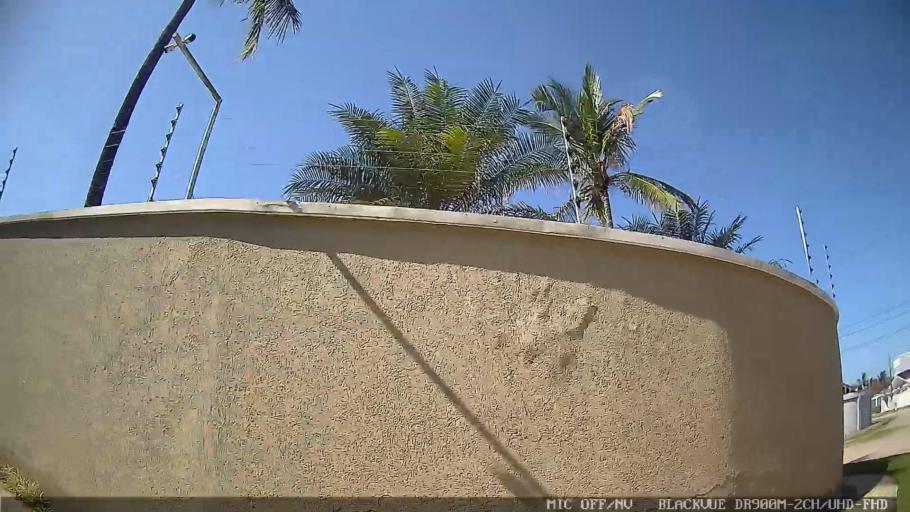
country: BR
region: Sao Paulo
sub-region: Guaruja
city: Guaruja
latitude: -23.9807
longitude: -46.2147
